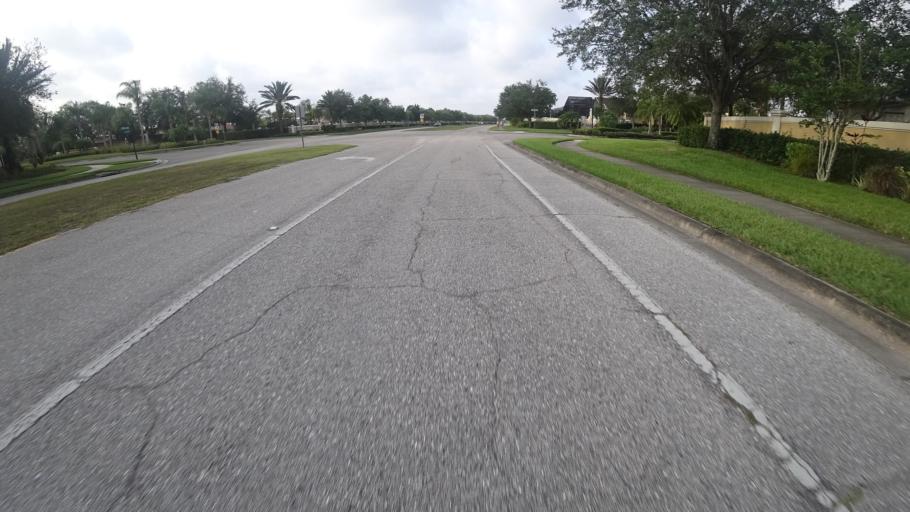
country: US
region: Florida
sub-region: Sarasota County
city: North Sarasota
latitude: 27.4235
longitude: -82.5128
